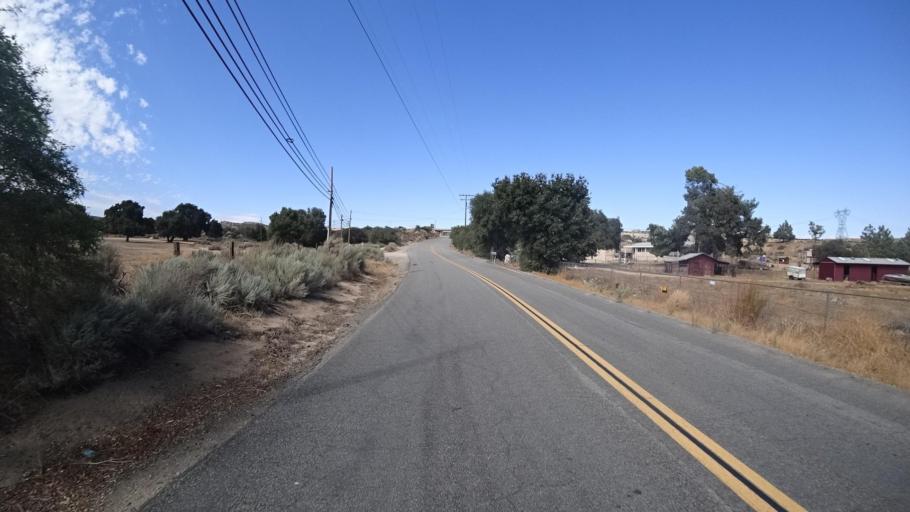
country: MX
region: Baja California
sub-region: Tecate
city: Cereso del Hongo
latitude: 32.6646
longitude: -116.2601
